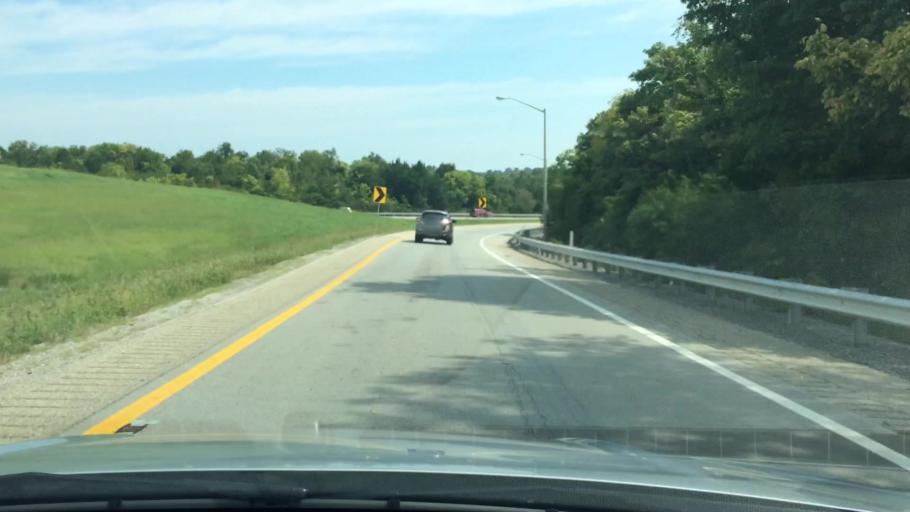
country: US
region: Kentucky
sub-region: Franklin County
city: Frankfort
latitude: 38.1568
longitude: -84.8909
